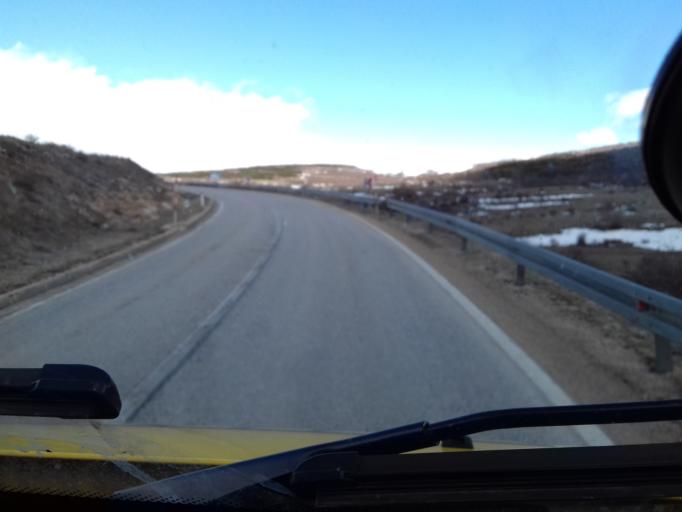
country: BA
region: Federation of Bosnia and Herzegovina
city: Tomislavgrad
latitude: 43.7651
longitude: 17.2378
